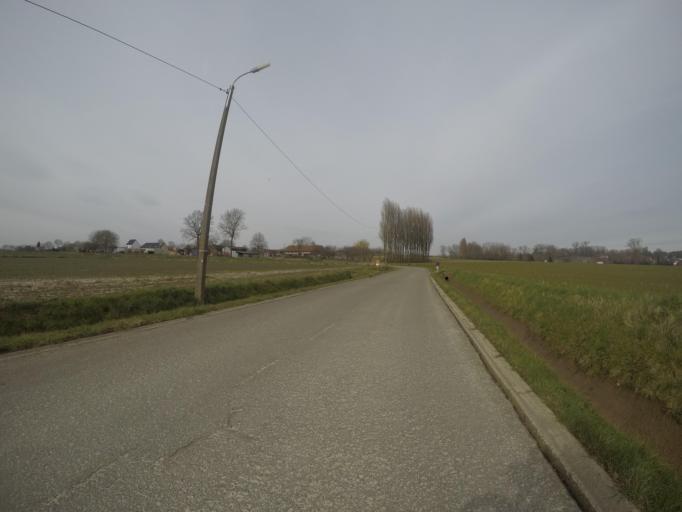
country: BE
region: Flanders
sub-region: Provincie Oost-Vlaanderen
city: Sint-Maria-Lierde
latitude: 50.8275
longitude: 3.8477
